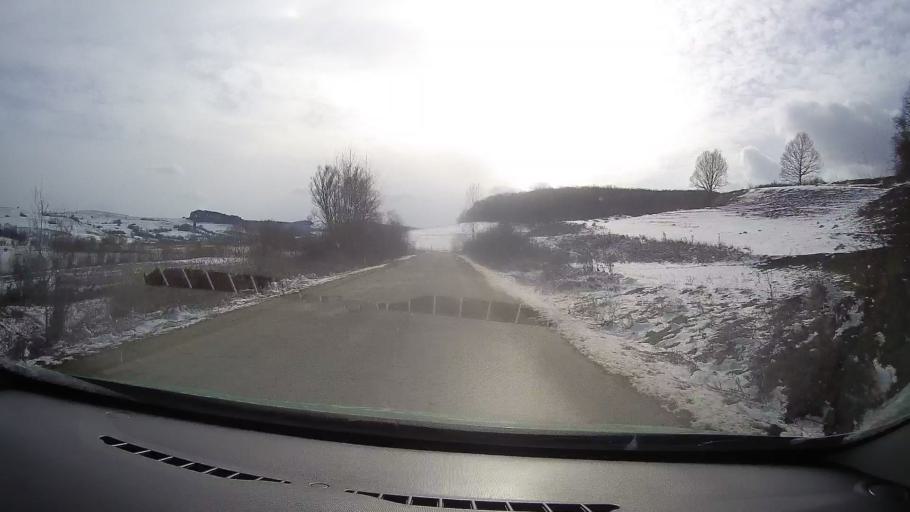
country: RO
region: Sibiu
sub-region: Comuna Bradeni
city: Bradeni
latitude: 46.0938
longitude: 24.8350
